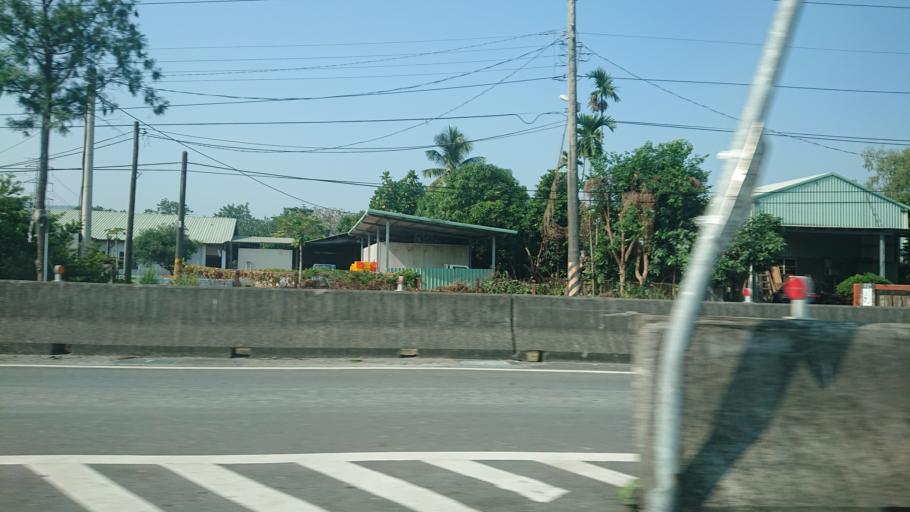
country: TW
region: Taiwan
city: Lugu
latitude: 23.7725
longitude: 120.6592
